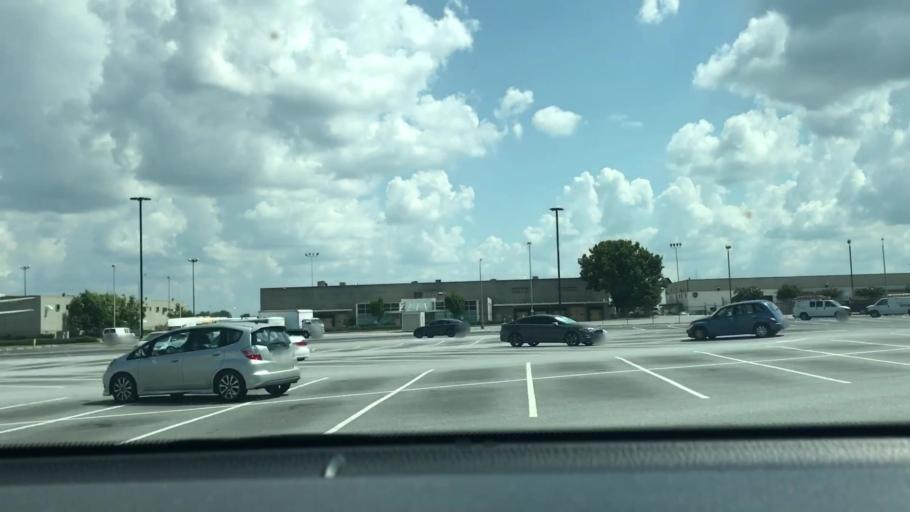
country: US
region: Georgia
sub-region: Fulton County
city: Hapeville
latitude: 33.6546
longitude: -84.4216
